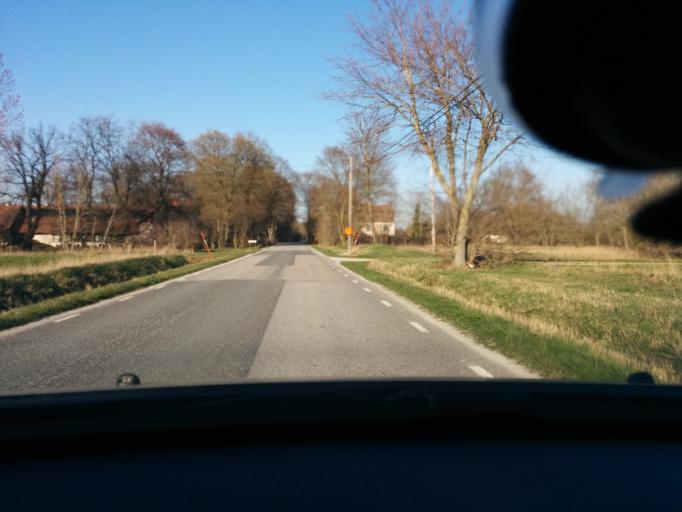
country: SE
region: Gotland
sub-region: Gotland
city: Hemse
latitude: 57.1641
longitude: 18.3662
